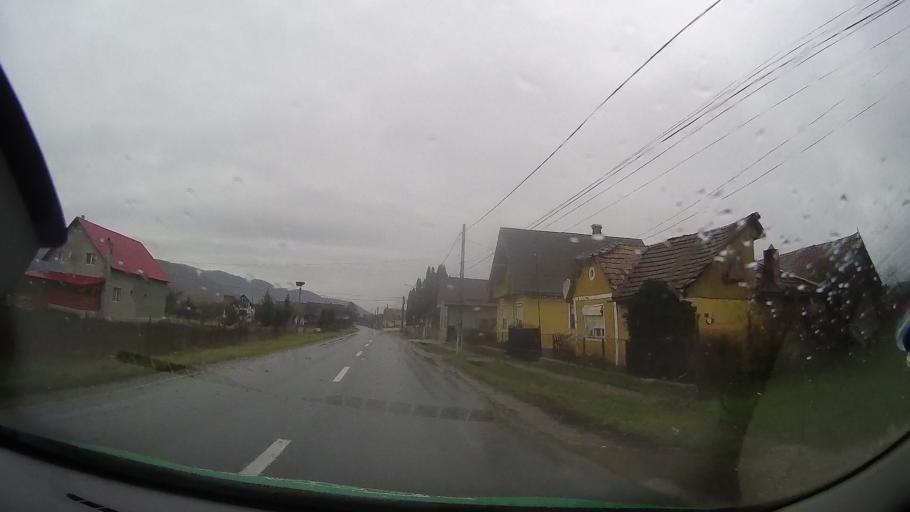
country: RO
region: Bistrita-Nasaud
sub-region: Comuna Mariselu
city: Mariselu
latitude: 47.0317
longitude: 24.4841
